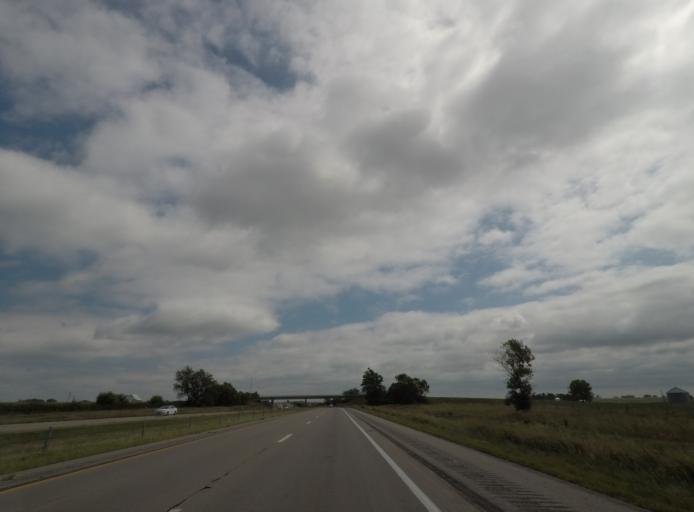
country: US
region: Iowa
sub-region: Jasper County
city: Newton
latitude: 41.6799
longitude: -92.9445
